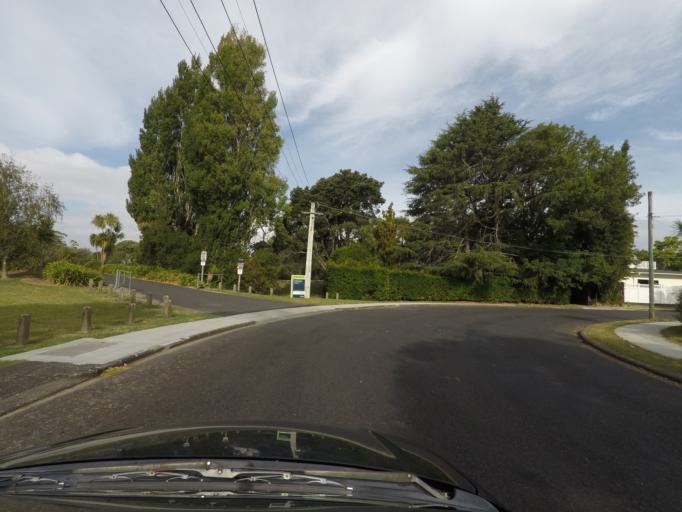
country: NZ
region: Auckland
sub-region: Auckland
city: Rosebank
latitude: -36.8968
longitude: 174.6710
